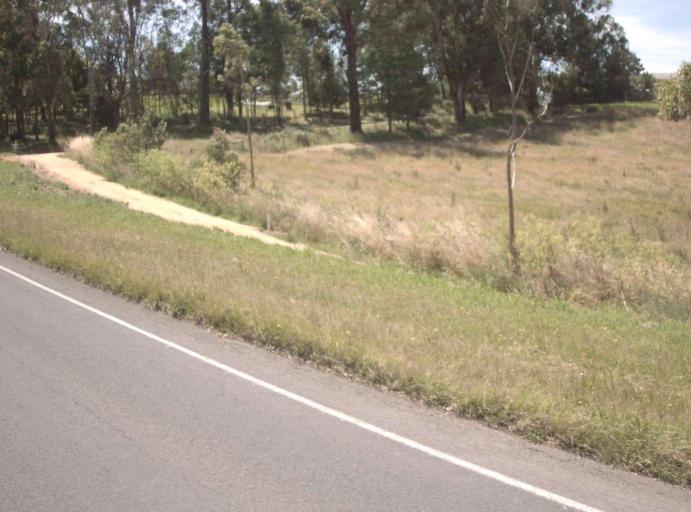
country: AU
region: Victoria
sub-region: Baw Baw
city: Warragul
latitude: -38.0416
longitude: 145.9524
